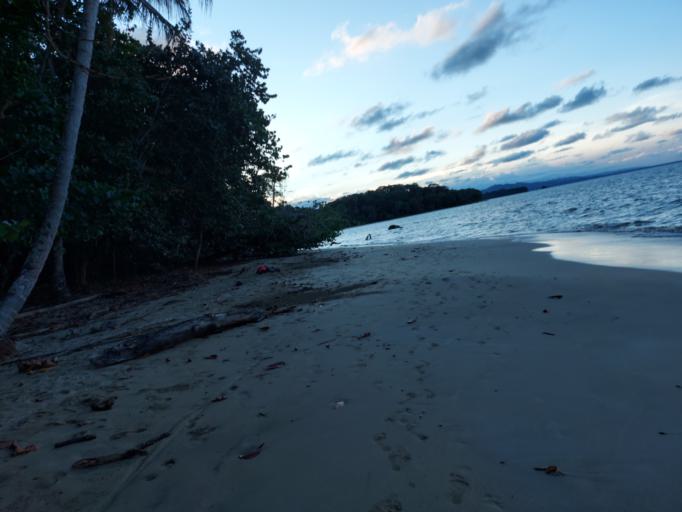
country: PA
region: Bocas del Toro
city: Barranco
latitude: 9.6426
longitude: -82.7135
